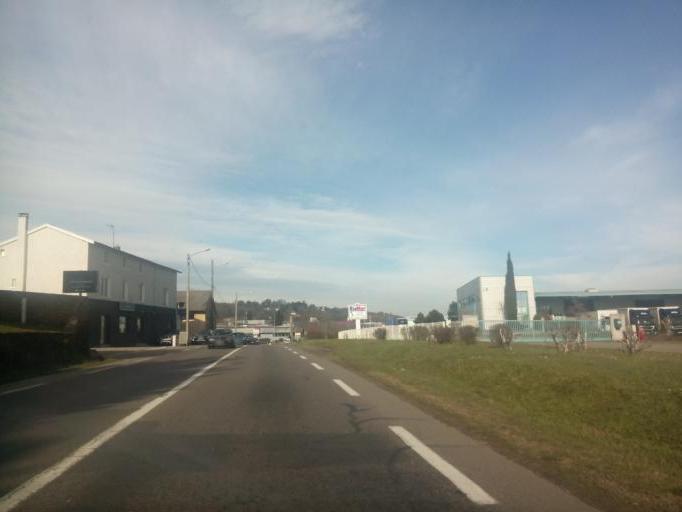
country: FR
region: Rhone-Alpes
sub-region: Departement du Rhone
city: Chaponost
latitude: 45.6955
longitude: 4.7666
